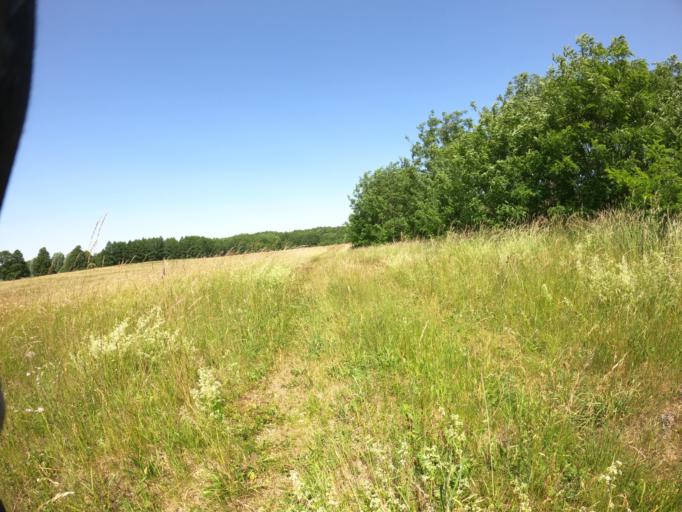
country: PL
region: West Pomeranian Voivodeship
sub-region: Powiat mysliborski
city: Mysliborz
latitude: 52.8916
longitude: 14.8088
